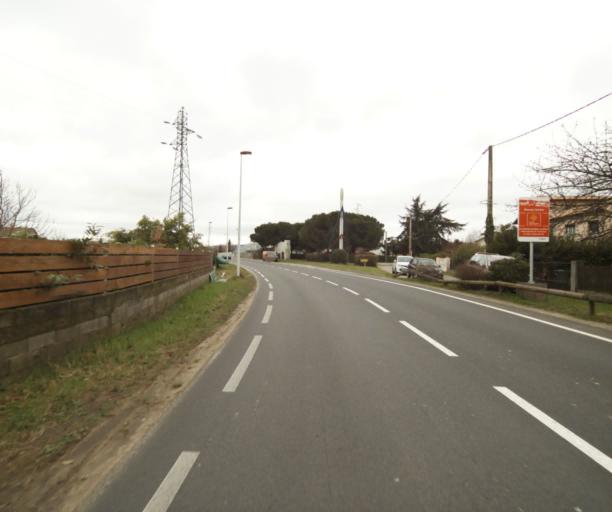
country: FR
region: Midi-Pyrenees
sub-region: Departement de l'Ariege
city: Pamiers
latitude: 43.1320
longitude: 1.6233
